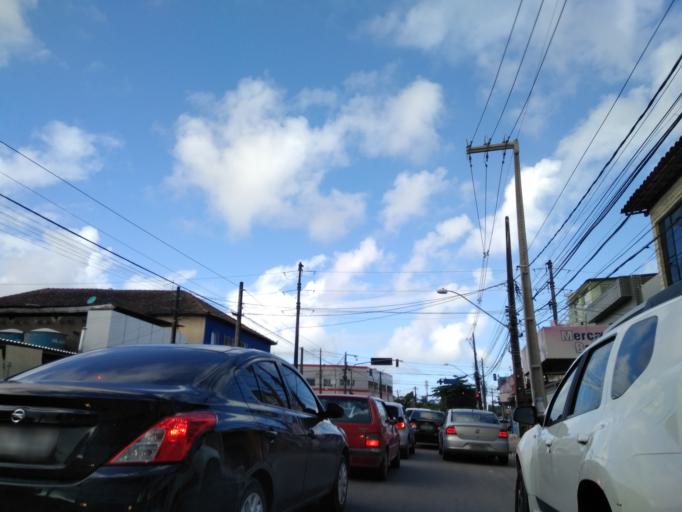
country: BR
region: Pernambuco
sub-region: Recife
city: Recife
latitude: -8.0751
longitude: -34.9190
